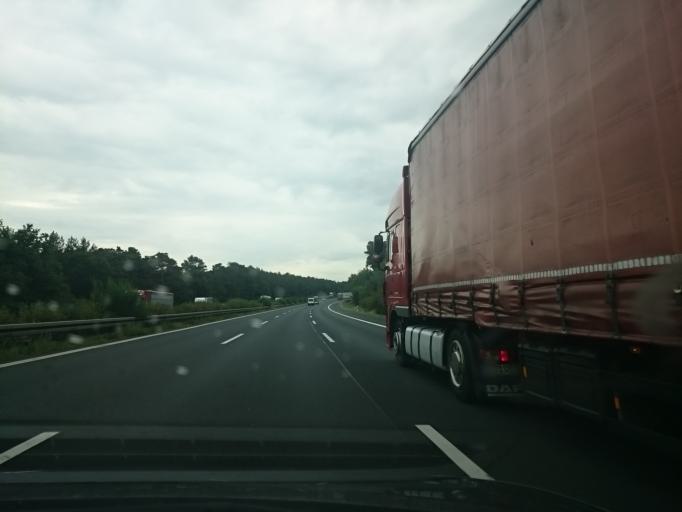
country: DE
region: Brandenburg
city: Beelitz
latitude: 52.2335
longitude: 12.9166
